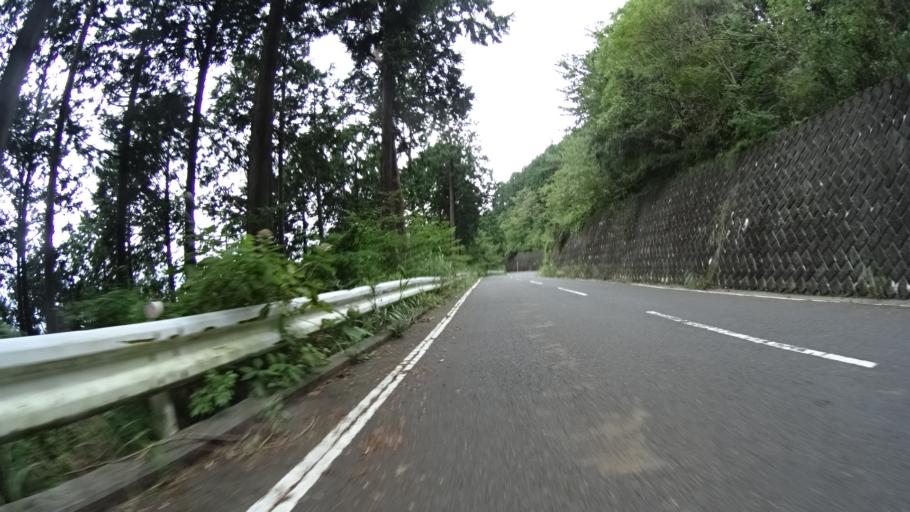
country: JP
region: Kanagawa
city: Hadano
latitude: 35.4160
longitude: 139.2142
